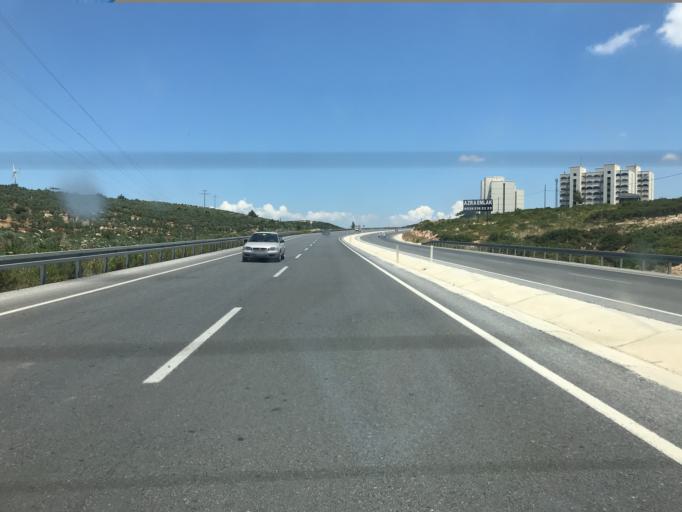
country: TR
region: Aydin
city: Akkoy
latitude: 37.4730
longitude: 27.3393
